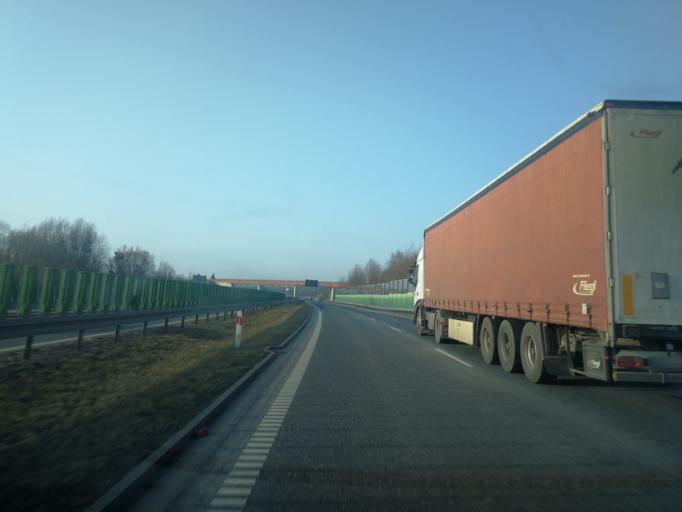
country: PL
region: Warmian-Masurian Voivodeship
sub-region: Powiat elblaski
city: Gronowo Gorne
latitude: 54.1301
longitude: 19.4591
